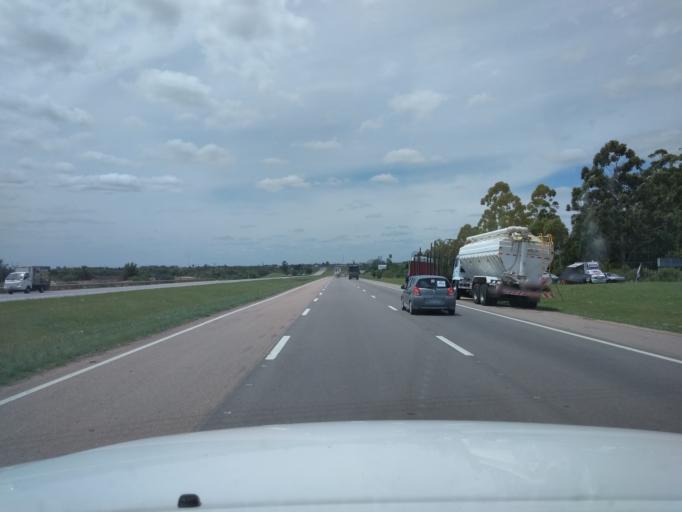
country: UY
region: Canelones
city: La Paz
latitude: -34.7607
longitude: -56.2618
